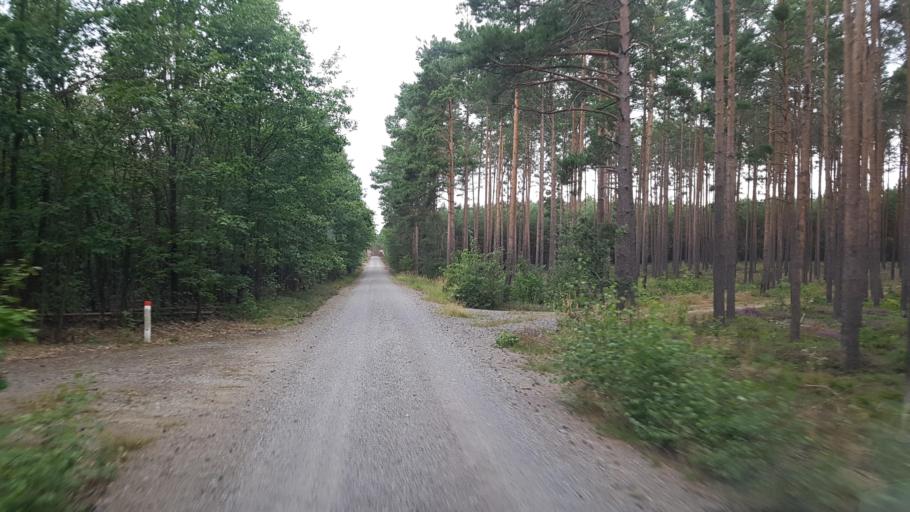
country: DE
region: Brandenburg
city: Schonborn
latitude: 51.6128
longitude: 13.5018
